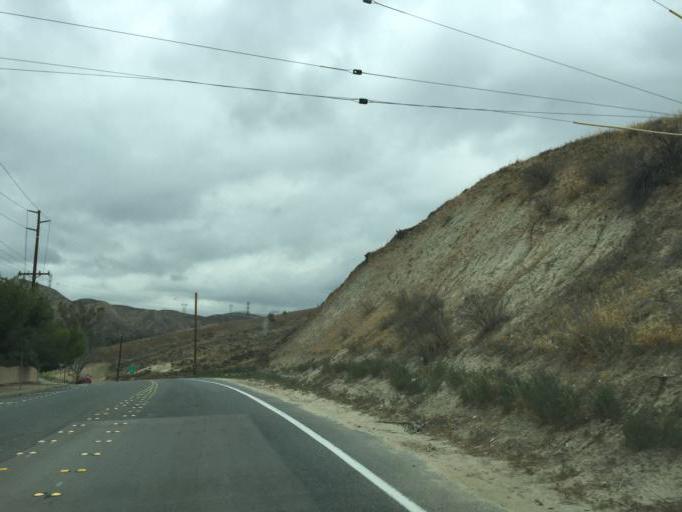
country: US
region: California
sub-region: Los Angeles County
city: Santa Clarita
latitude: 34.4540
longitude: -118.4956
